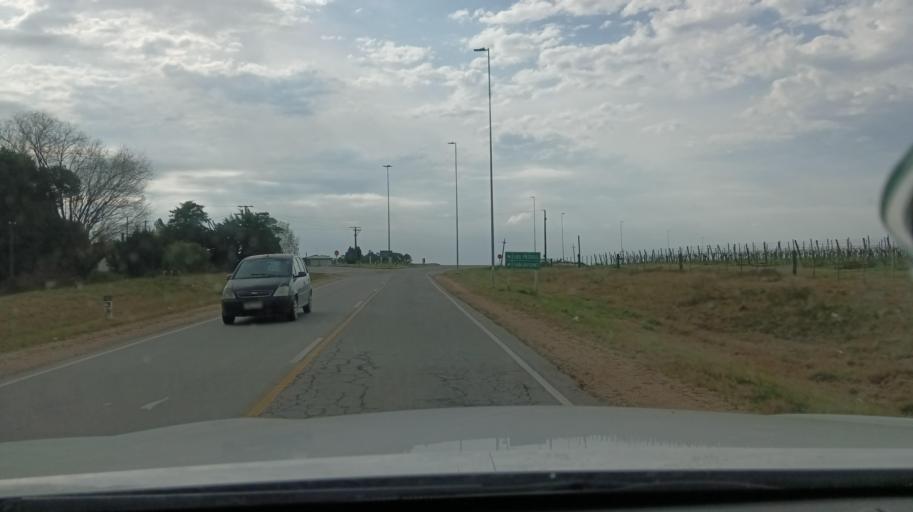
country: UY
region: Canelones
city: Sauce
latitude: -34.6681
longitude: -56.1144
